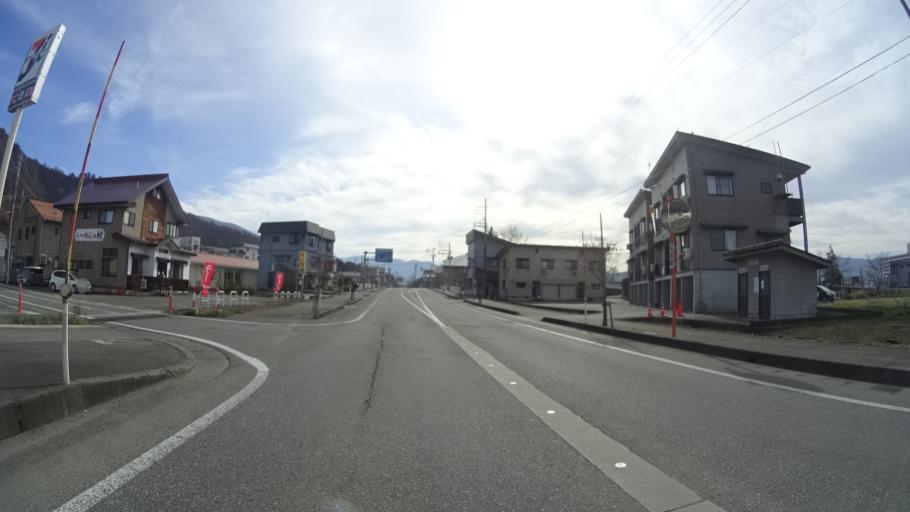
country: JP
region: Niigata
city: Muikamachi
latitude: 37.0636
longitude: 138.8827
